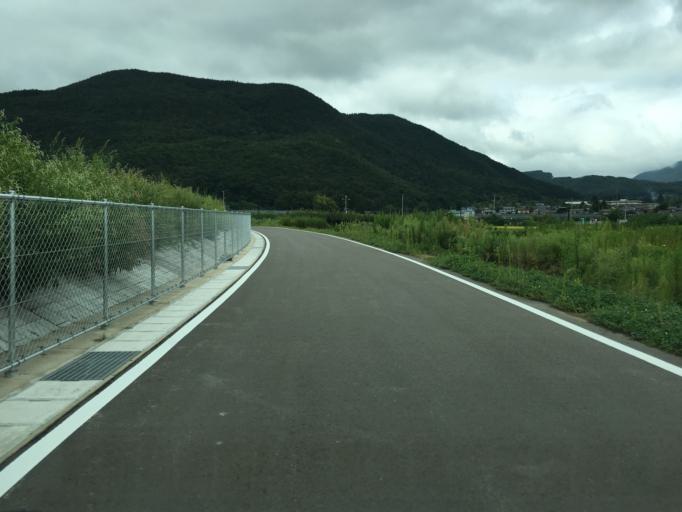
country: JP
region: Fukushima
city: Fukushima-shi
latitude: 37.8046
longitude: 140.4129
